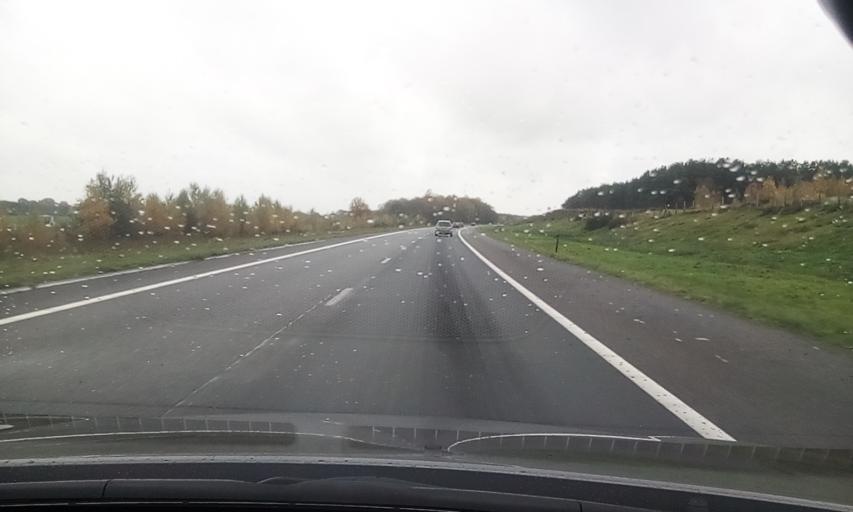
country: NL
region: Drenthe
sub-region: Gemeente Hoogeveen
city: Hoogeveen
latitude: 52.8056
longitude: 6.4580
